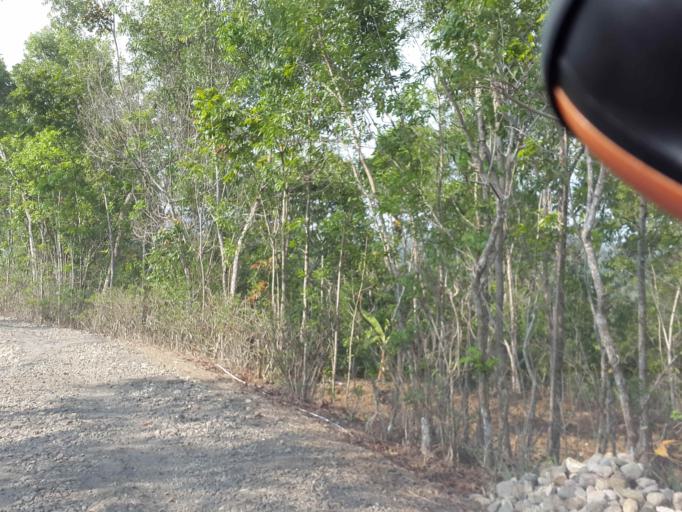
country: ID
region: East Java
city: Krajan
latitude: -8.0933
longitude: 111.0279
